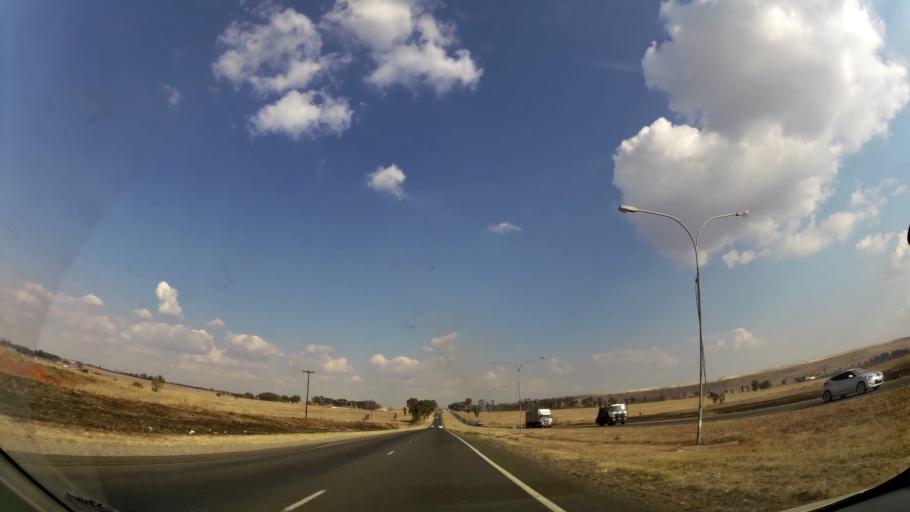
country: ZA
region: Gauteng
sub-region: Ekurhuleni Metropolitan Municipality
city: Brakpan
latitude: -26.3205
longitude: 28.3382
